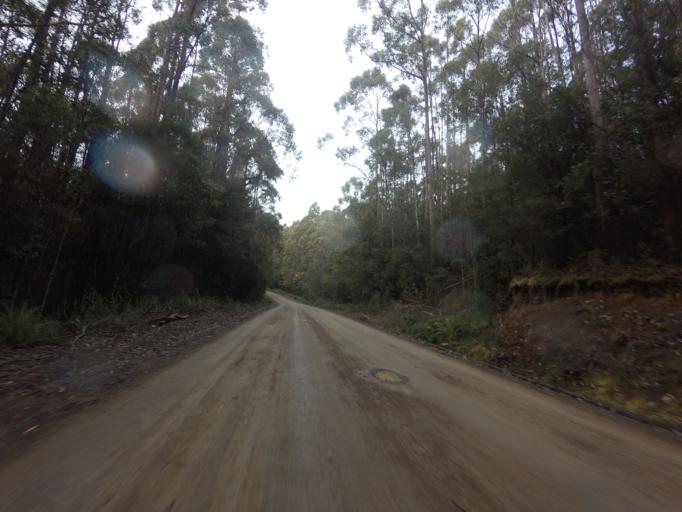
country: AU
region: Tasmania
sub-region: Huon Valley
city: Geeveston
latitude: -43.5247
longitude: 146.8830
